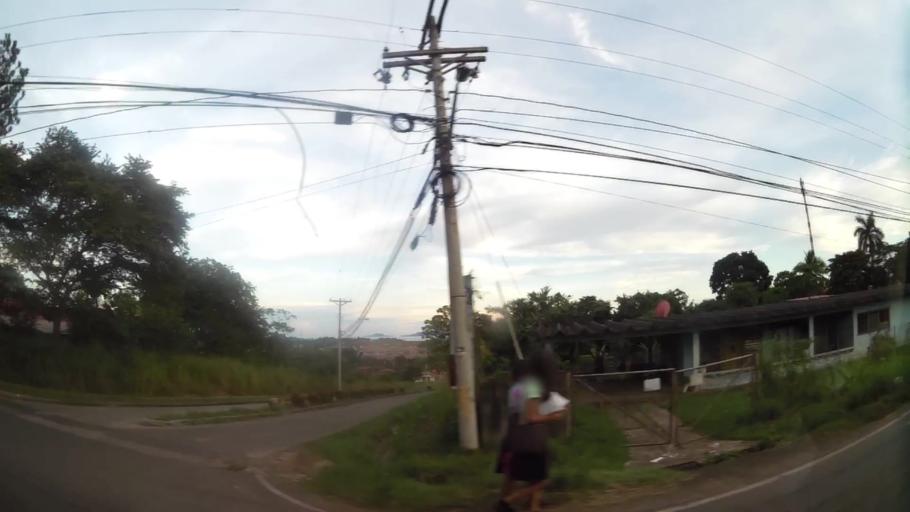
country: PA
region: Panama
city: La Chorrera
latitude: 8.8629
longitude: -79.7659
